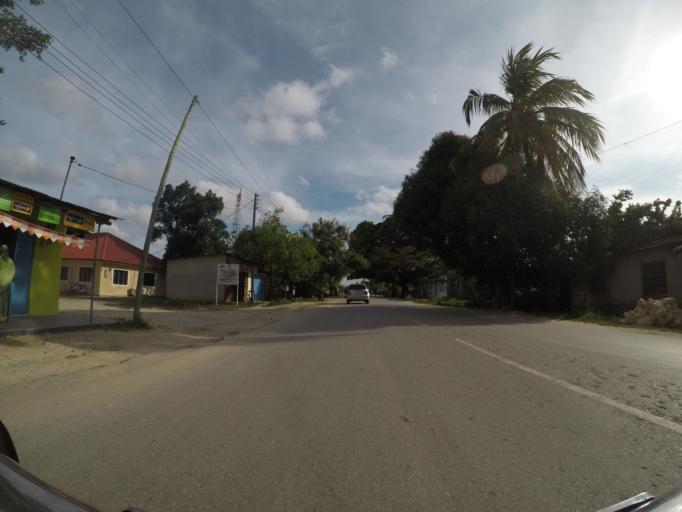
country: TZ
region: Pemba South
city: Chake Chake
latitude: -5.2273
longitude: 39.7755
